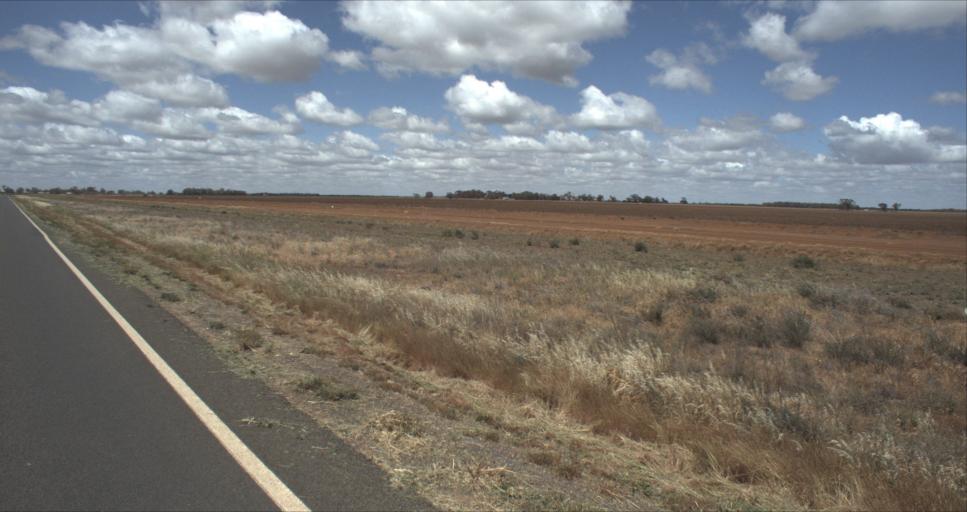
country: AU
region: New South Wales
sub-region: Murrumbidgee Shire
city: Darlington Point
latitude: -34.4716
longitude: 146.1415
